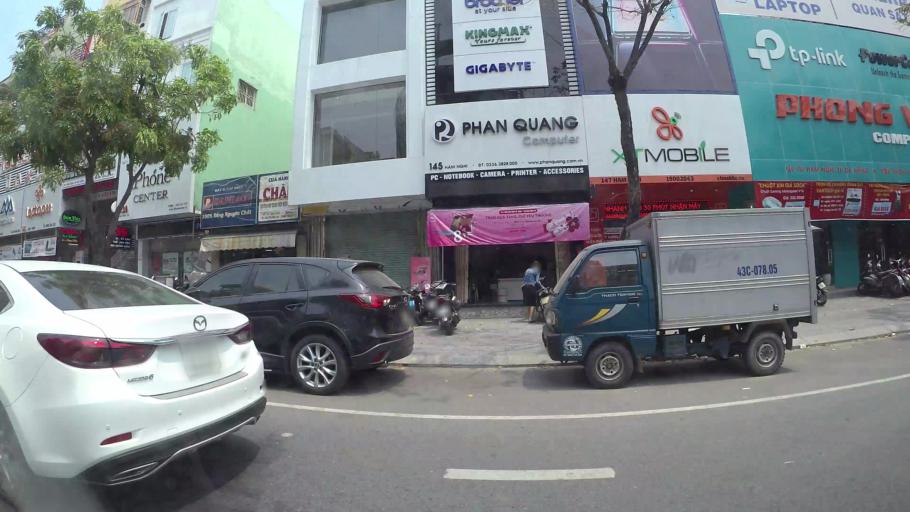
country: VN
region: Da Nang
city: Da Nang
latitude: 16.0611
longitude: 108.2110
